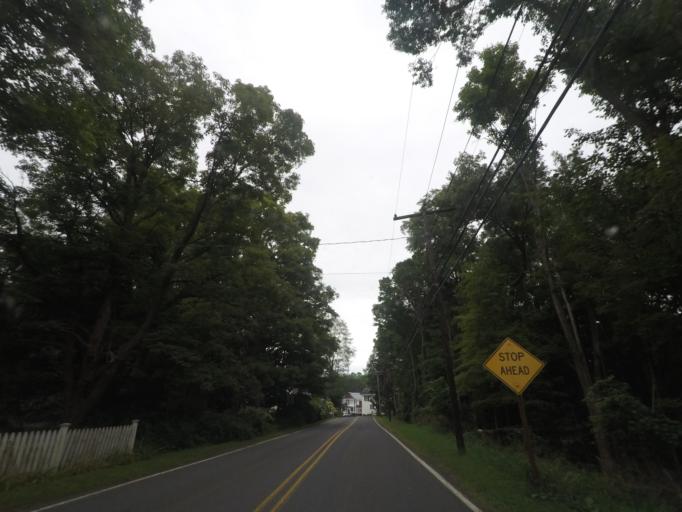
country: US
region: New York
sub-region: Columbia County
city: Chatham
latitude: 42.4420
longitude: -73.5637
